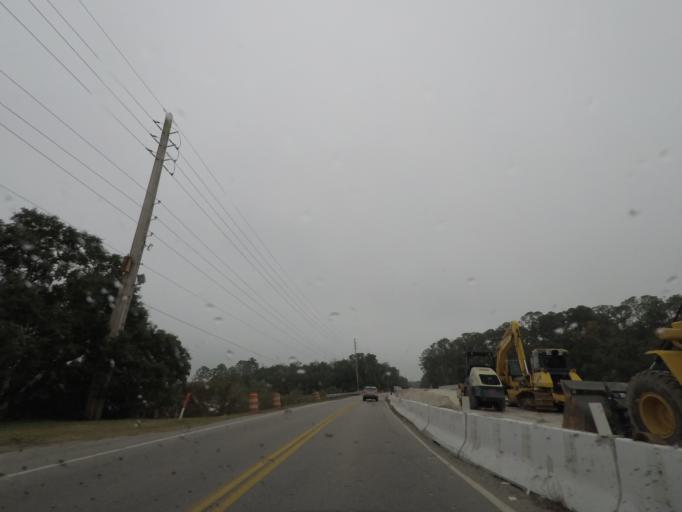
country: US
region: South Carolina
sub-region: Charleston County
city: Seabrook Island
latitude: 32.5598
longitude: -80.2798
